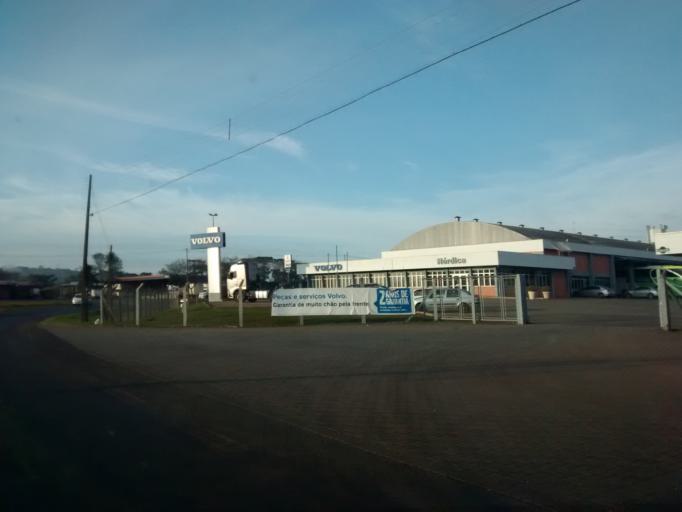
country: BR
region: Parana
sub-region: Francisco Beltrao
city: Francisco Beltrao
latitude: -26.1521
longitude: -53.0232
